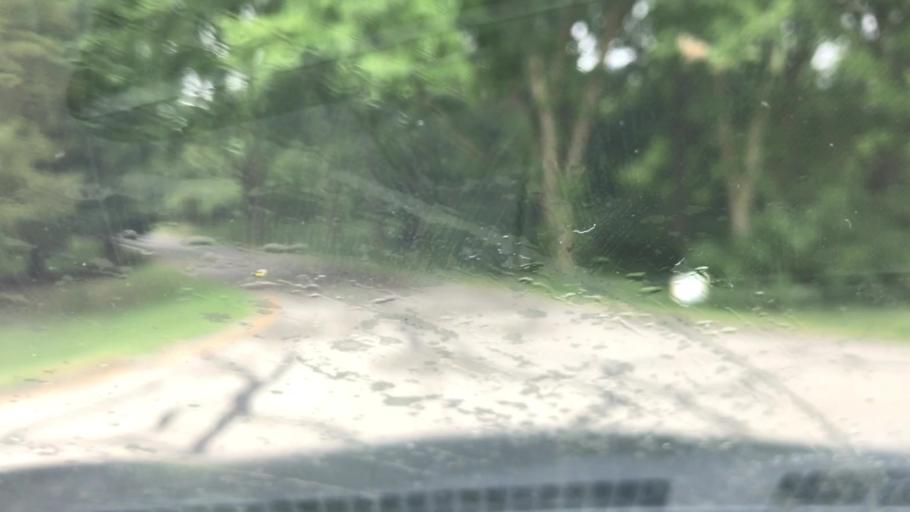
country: US
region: Michigan
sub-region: Oakland County
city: South Lyon
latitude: 42.5110
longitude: -83.6855
